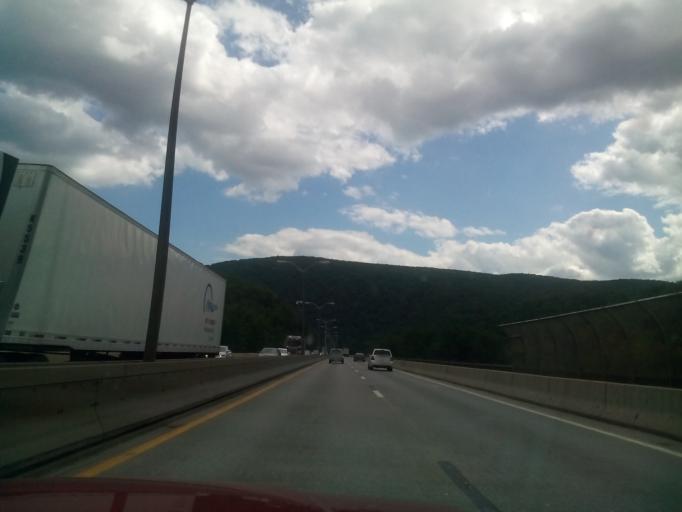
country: US
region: Pennsylvania
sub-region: Monroe County
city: East Stroudsburg
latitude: 40.9806
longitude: -75.1369
